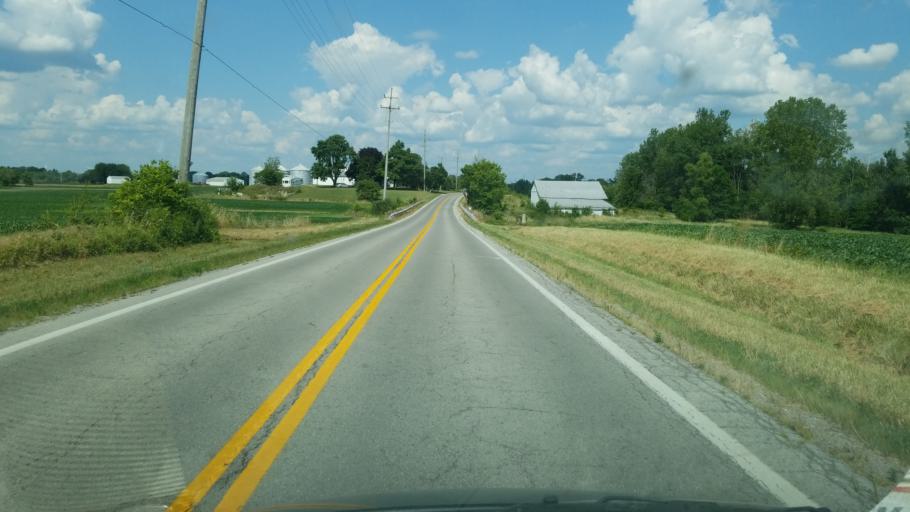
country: US
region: Ohio
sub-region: Marion County
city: Marion
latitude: 40.5446
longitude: -83.1982
